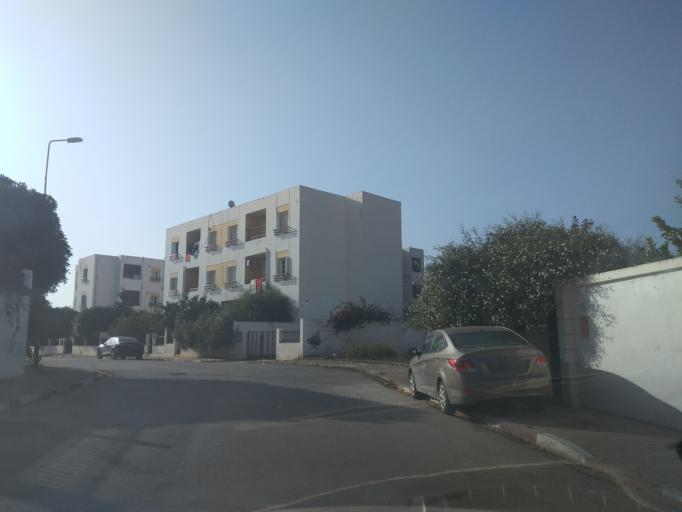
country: TN
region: Manouba
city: Manouba
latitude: 36.7896
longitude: 10.0856
